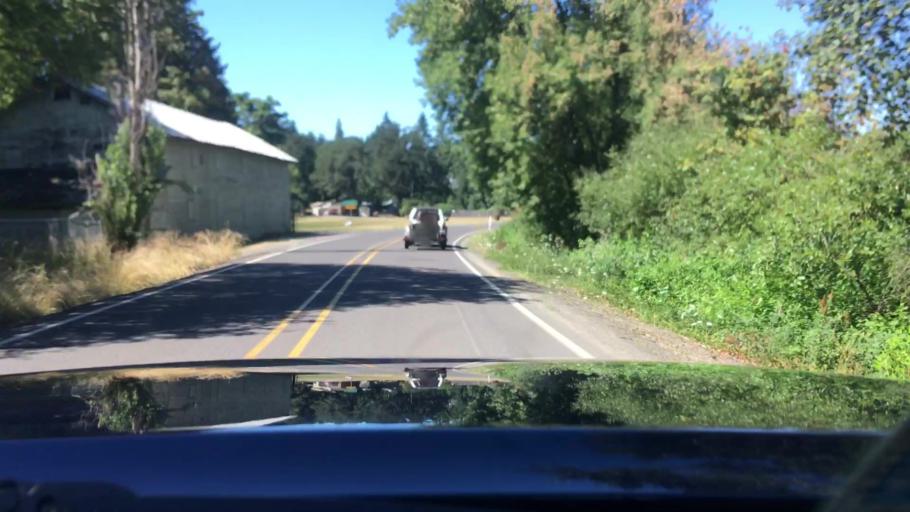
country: US
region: Oregon
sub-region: Lane County
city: Cottage Grove
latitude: 43.8297
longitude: -123.0450
